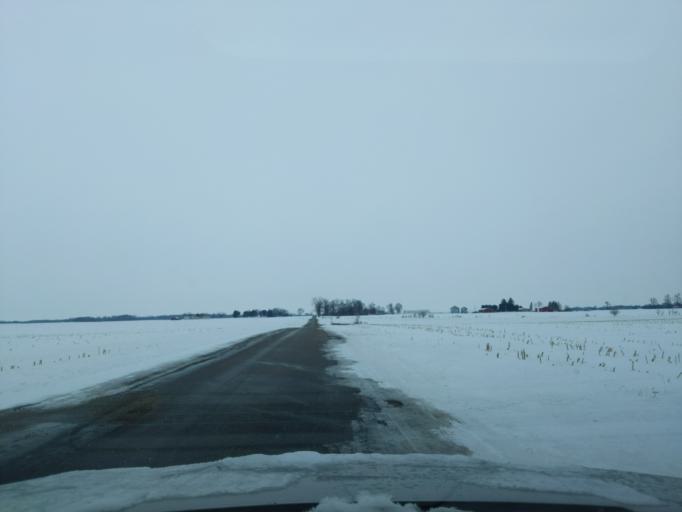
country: US
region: Indiana
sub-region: Benton County
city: Otterbein
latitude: 40.4355
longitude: -87.0927
